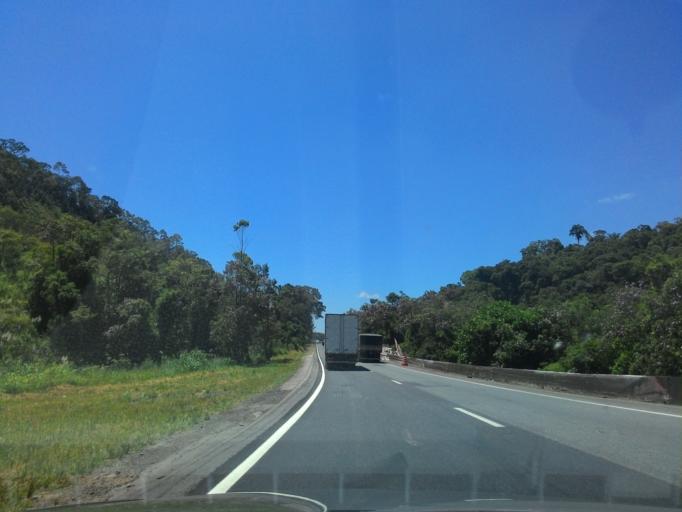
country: BR
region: Parana
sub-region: Antonina
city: Antonina
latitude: -25.1054
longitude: -48.7160
